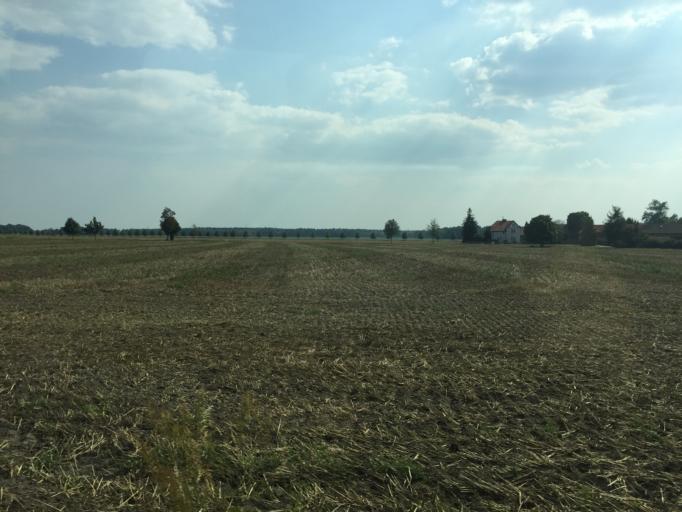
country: DE
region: Brandenburg
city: Welzow
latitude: 51.5532
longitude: 14.1940
